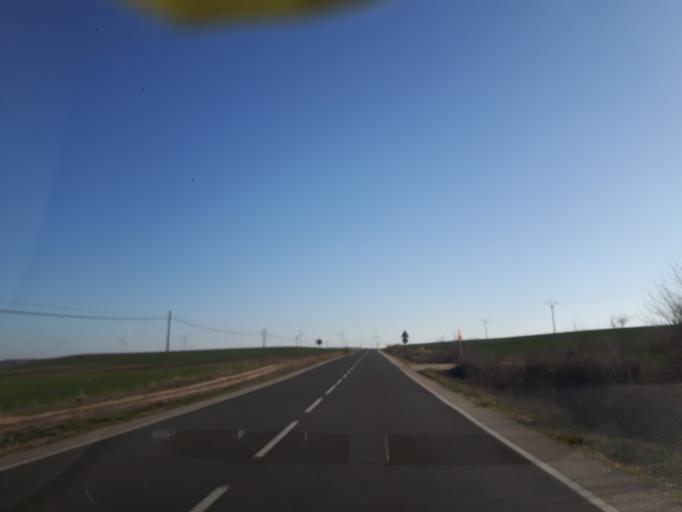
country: ES
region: Castille and Leon
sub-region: Provincia de Salamanca
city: Garcihernandez
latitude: 40.8478
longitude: -5.4577
